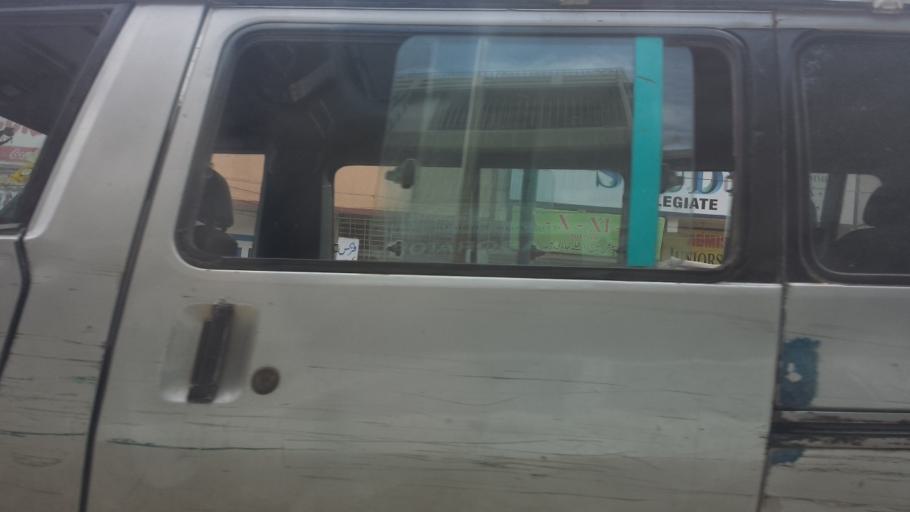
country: PK
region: Sindh
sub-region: Karachi District
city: Karachi
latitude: 24.9268
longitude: 67.0718
